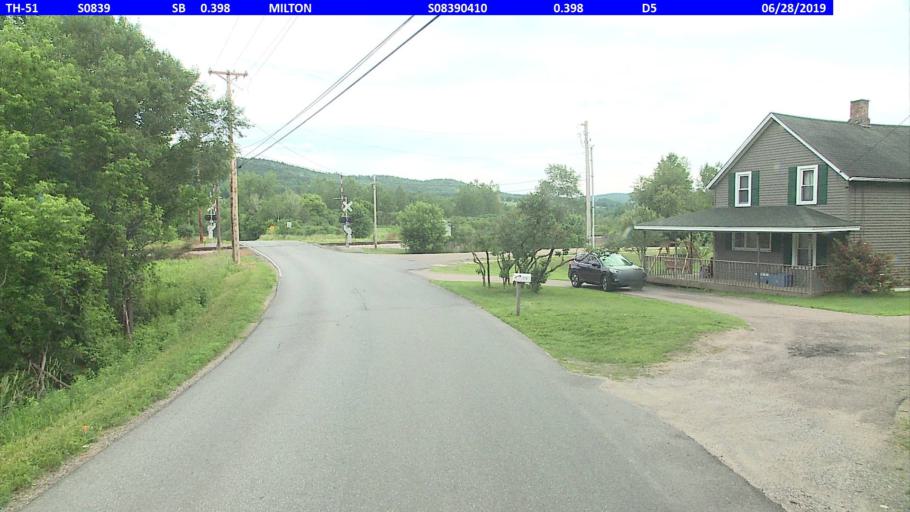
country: US
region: Vermont
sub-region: Chittenden County
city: Milton
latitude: 44.6098
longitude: -73.1097
